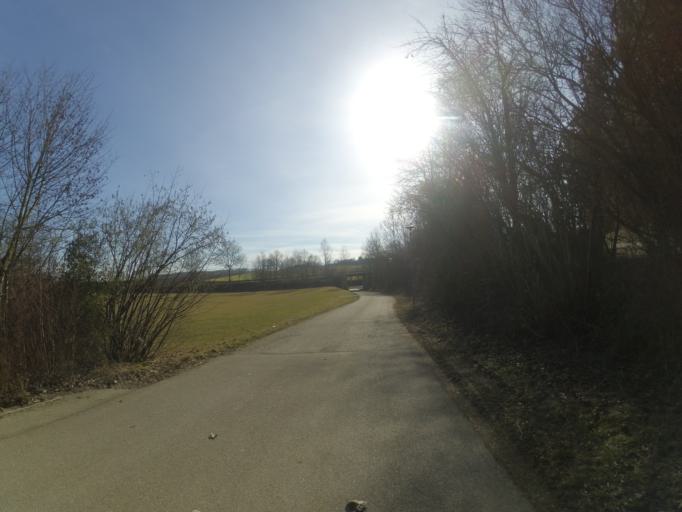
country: DE
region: Baden-Wuerttemberg
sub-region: Tuebingen Region
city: Bernstadt
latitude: 48.4841
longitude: 10.0638
